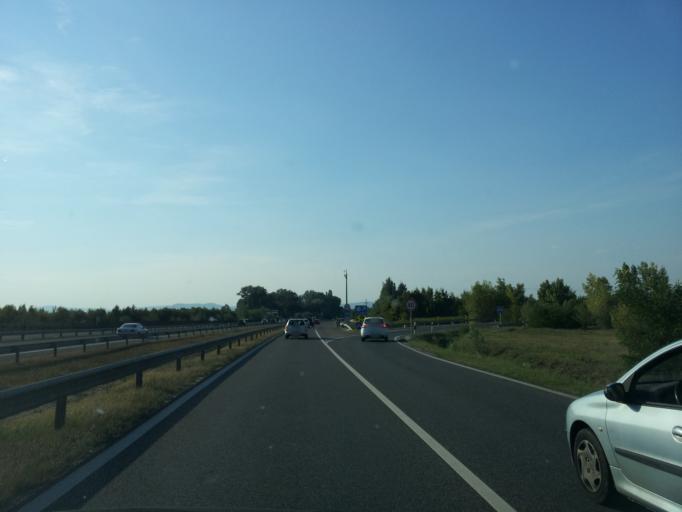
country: HU
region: Budapest
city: Budapest XV. keruelet
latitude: 47.5813
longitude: 19.1491
